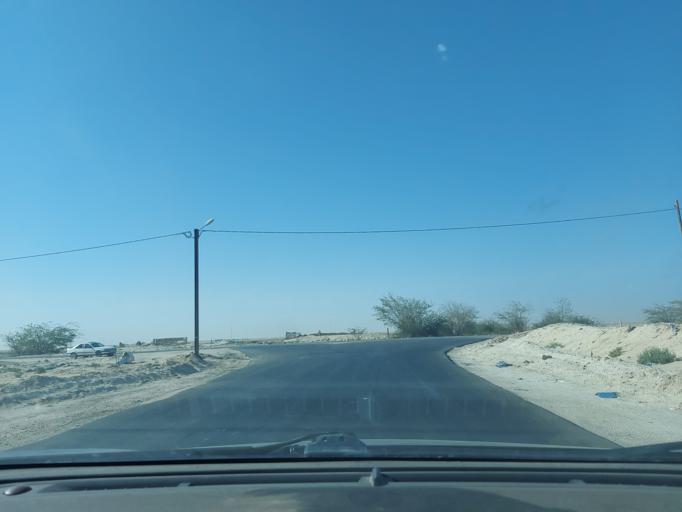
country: MR
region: Nouakchott
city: Nouakchott
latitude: 17.9928
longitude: -15.9882
